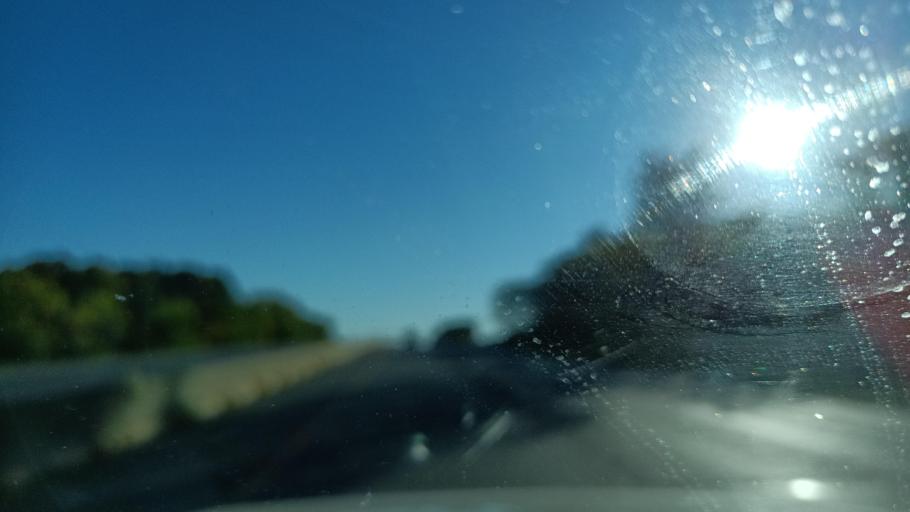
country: US
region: Missouri
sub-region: Boone County
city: Columbia
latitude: 38.9310
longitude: -92.3026
